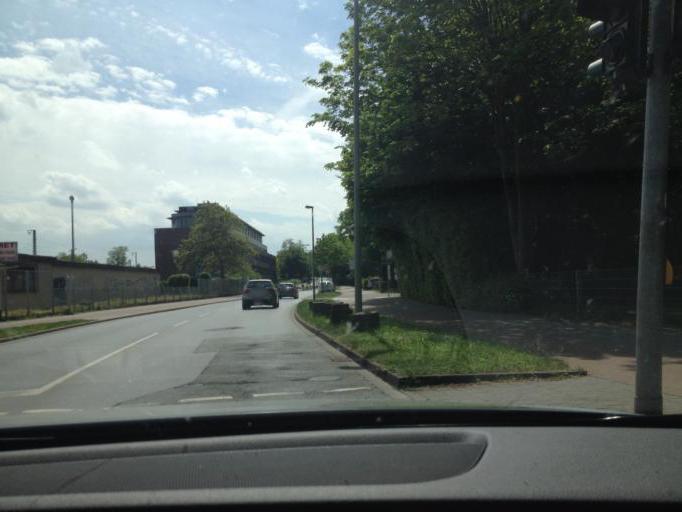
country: DE
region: North Rhine-Westphalia
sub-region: Regierungsbezirk Dusseldorf
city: Hochfeld
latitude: 51.3654
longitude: 6.7763
